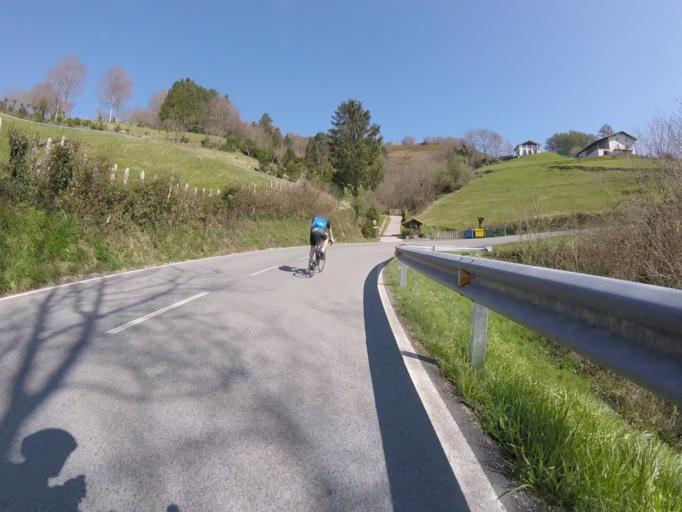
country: ES
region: Navarre
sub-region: Provincia de Navarra
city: Leitza
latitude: 43.0889
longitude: -1.9018
